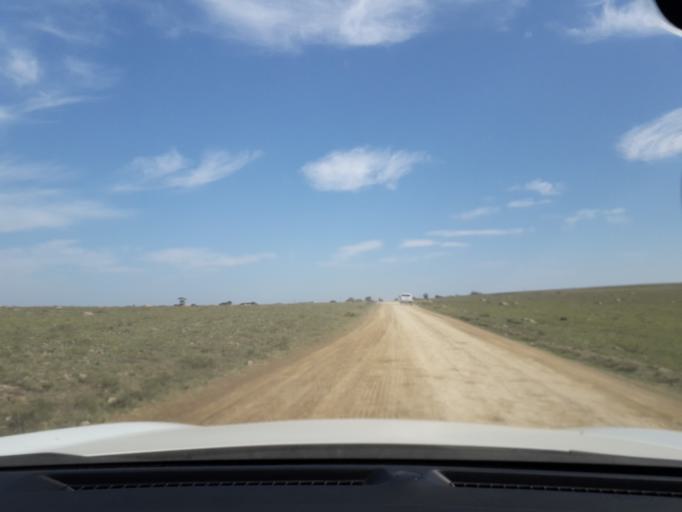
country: ZA
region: Eastern Cape
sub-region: Buffalo City Metropolitan Municipality
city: Bhisho
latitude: -33.0056
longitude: 27.3125
